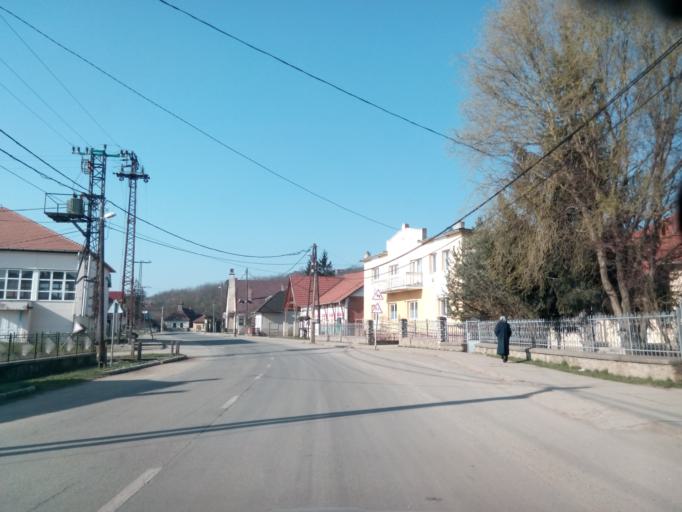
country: HU
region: Borsod-Abauj-Zemplen
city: Szendro
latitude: 48.5370
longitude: 20.7335
